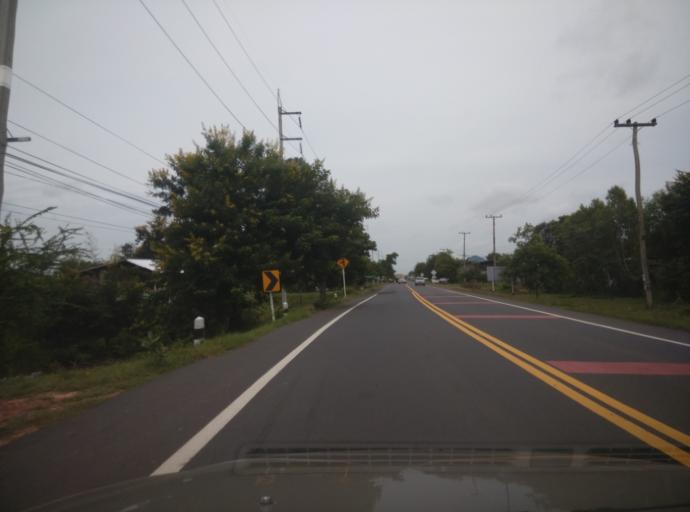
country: TH
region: Sisaket
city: Uthumphon Phisai
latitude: 15.0735
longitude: 104.0985
